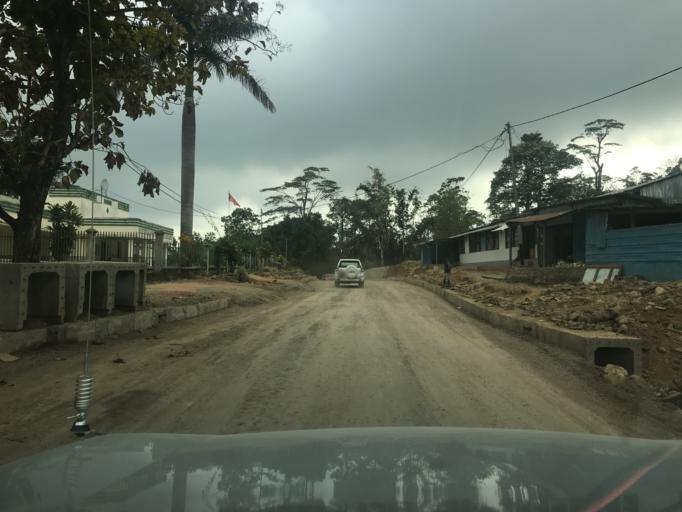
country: TL
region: Ainaro
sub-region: Ainaro
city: Ainaro
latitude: -8.9941
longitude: 125.5075
